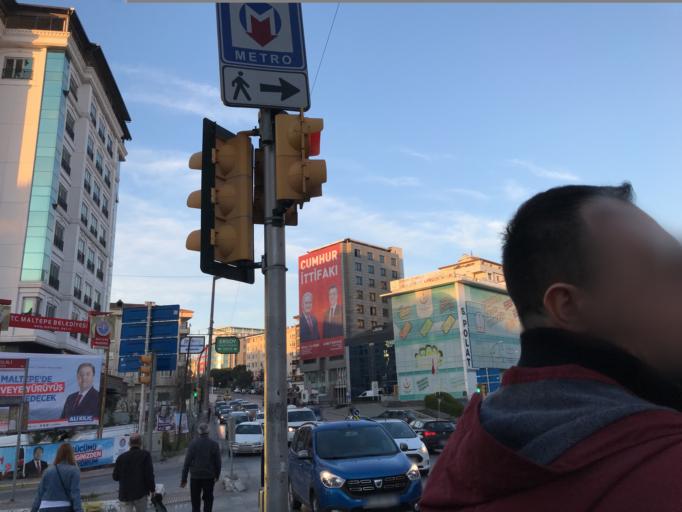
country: TR
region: Istanbul
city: Maltepe
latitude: 40.9327
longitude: 29.1366
